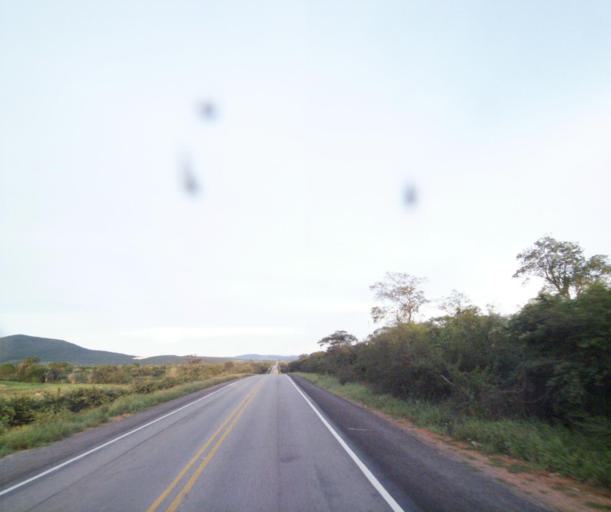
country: BR
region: Bahia
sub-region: Brumado
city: Brumado
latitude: -14.2578
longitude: -41.7772
